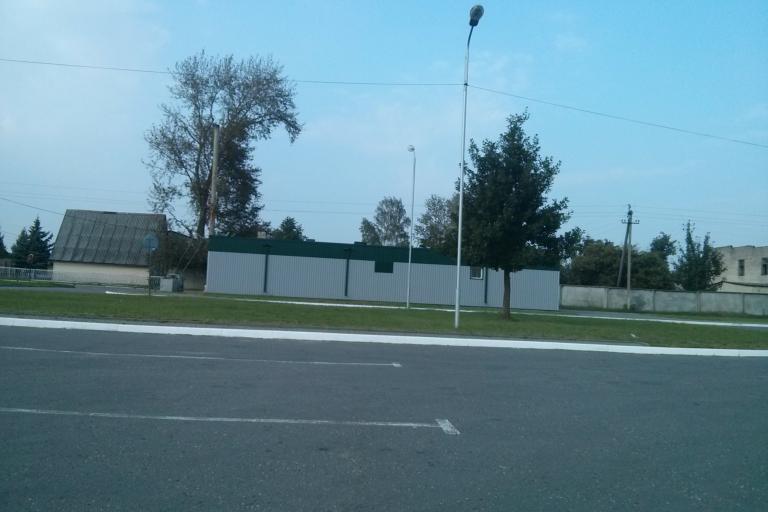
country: BY
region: Minsk
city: Chervyen'
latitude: 53.7213
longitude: 28.4175
